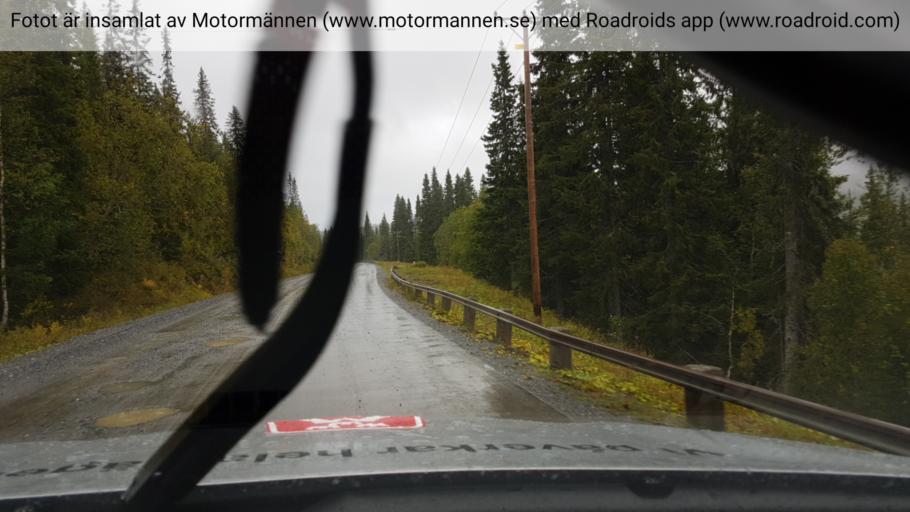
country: SE
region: Jaemtland
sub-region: Are Kommun
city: Are
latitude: 63.6778
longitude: 12.8165
